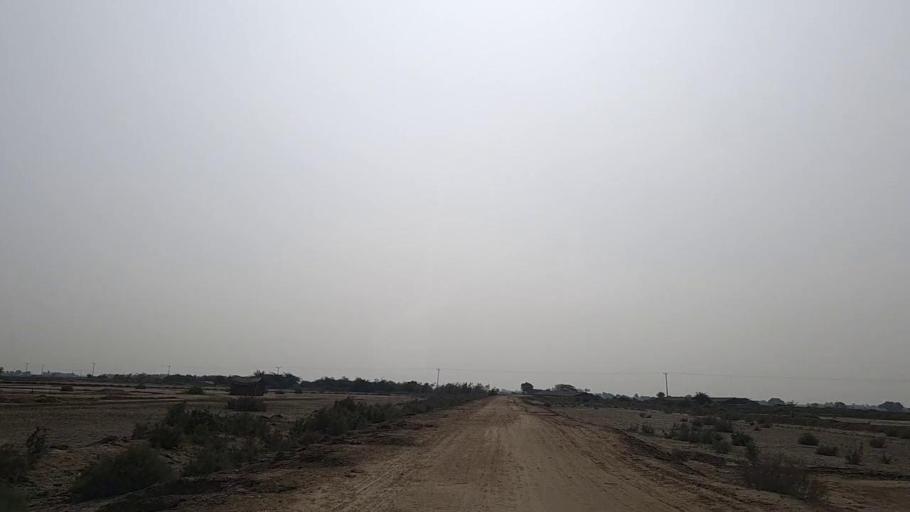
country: PK
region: Sindh
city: Mirpur Sakro
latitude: 24.6314
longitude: 67.7677
